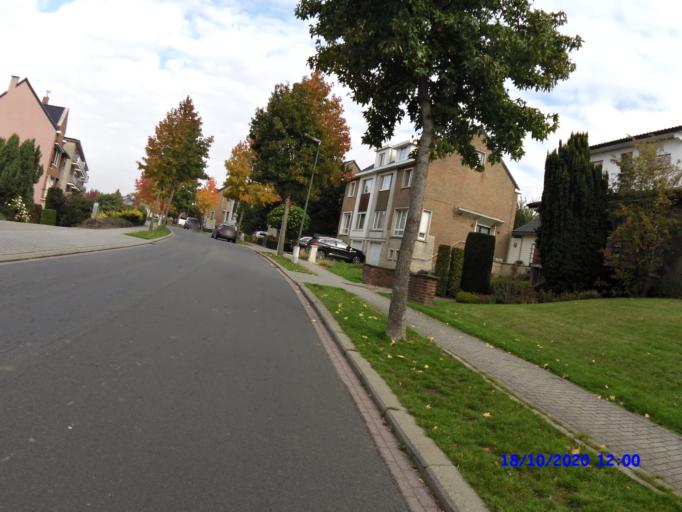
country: BE
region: Flanders
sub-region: Provincie Vlaams-Brabant
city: Landen
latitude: 50.7541
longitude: 5.0844
